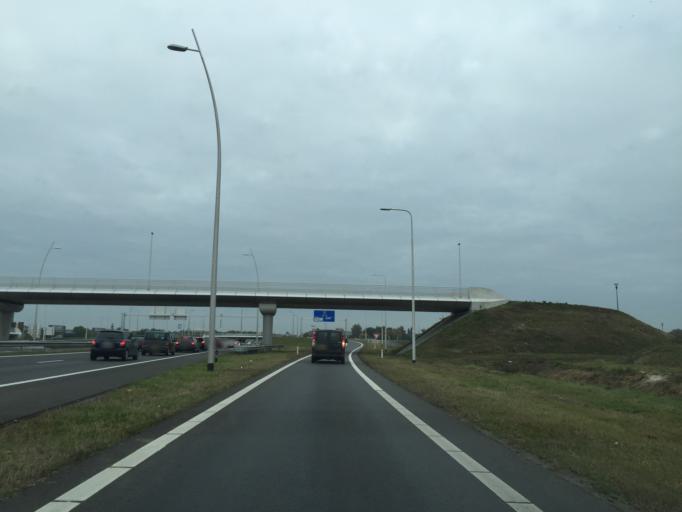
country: NL
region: North Brabant
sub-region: Gemeente Waalwijk
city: Waalwijk
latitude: 51.6779
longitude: 5.0489
